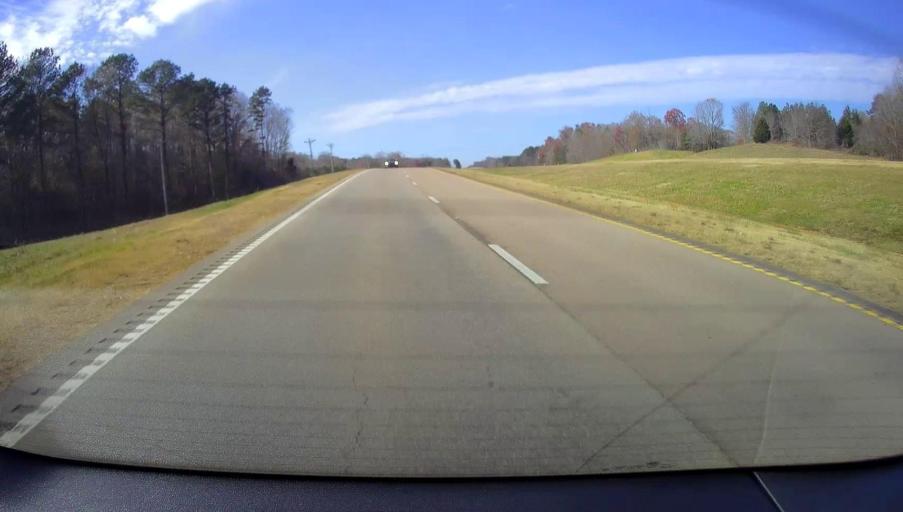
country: US
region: Mississippi
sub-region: Tippah County
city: Ripley
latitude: 34.9499
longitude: -88.8236
